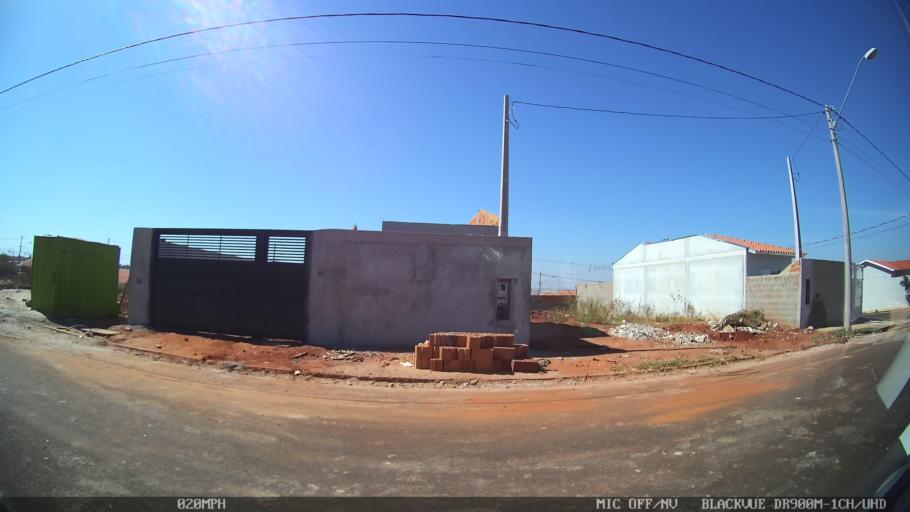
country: BR
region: Sao Paulo
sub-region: Sao Jose Do Rio Preto
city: Sao Jose do Rio Preto
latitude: -20.7539
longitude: -49.4246
